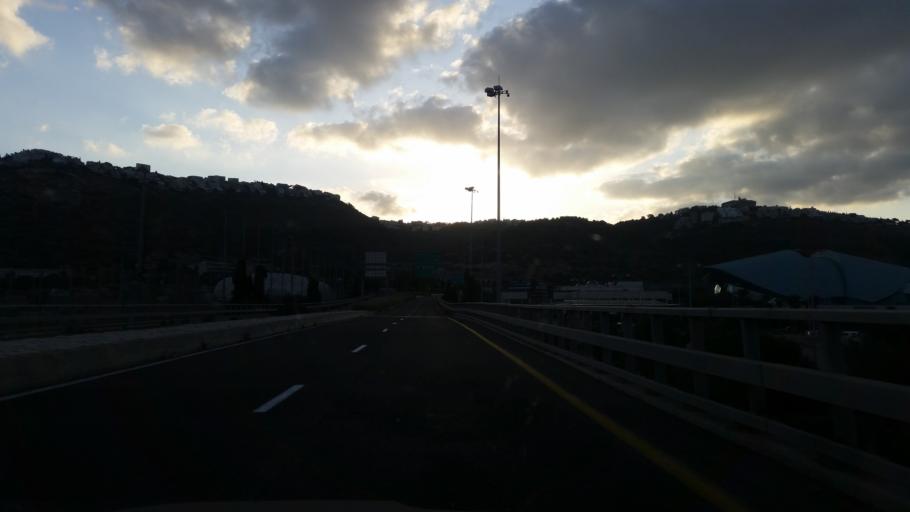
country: IL
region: Haifa
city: Tirat Karmel
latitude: 32.7926
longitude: 34.9621
